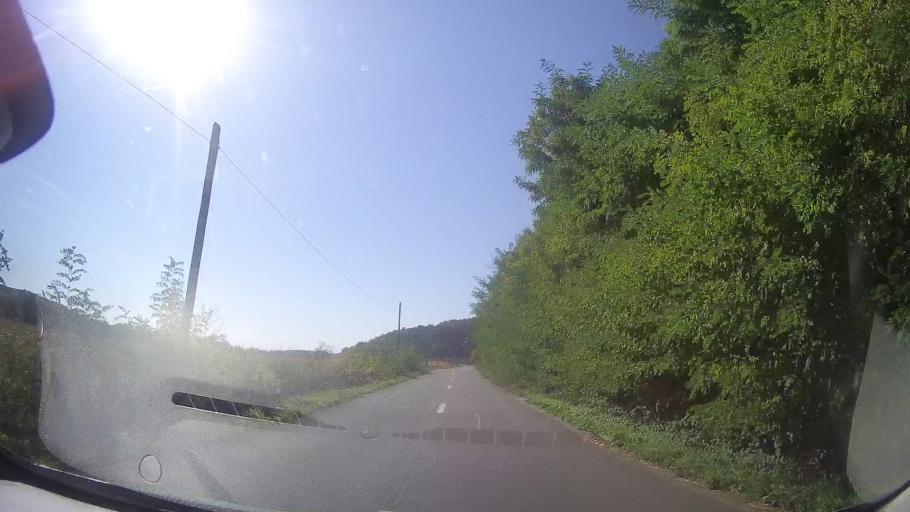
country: RO
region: Timis
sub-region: Comuna Ohaba Lunga
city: Ohaba Lunga
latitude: 45.8857
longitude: 21.9665
